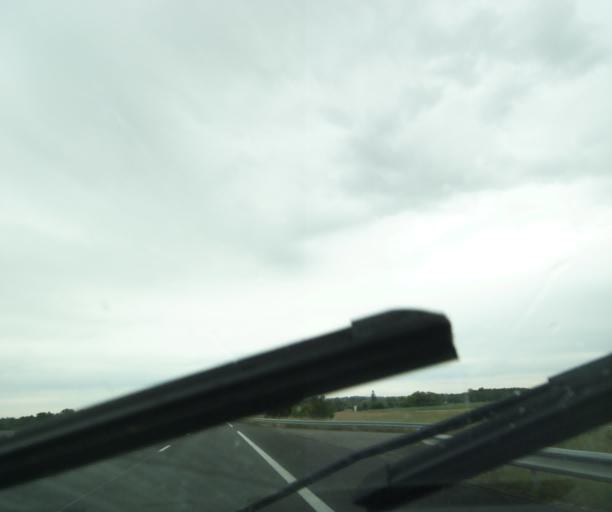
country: FR
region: Midi-Pyrenees
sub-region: Departement du Tarn-et-Garonne
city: Realville
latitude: 44.1079
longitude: 1.4612
